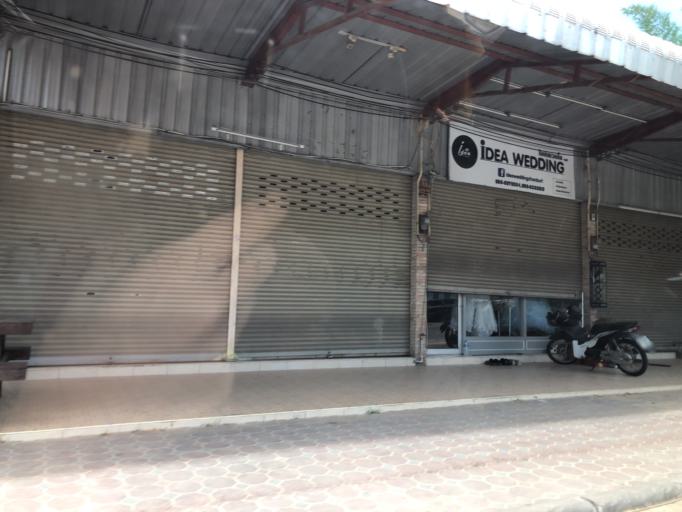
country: TH
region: Chon Buri
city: Phatthaya
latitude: 12.9540
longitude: 100.8989
